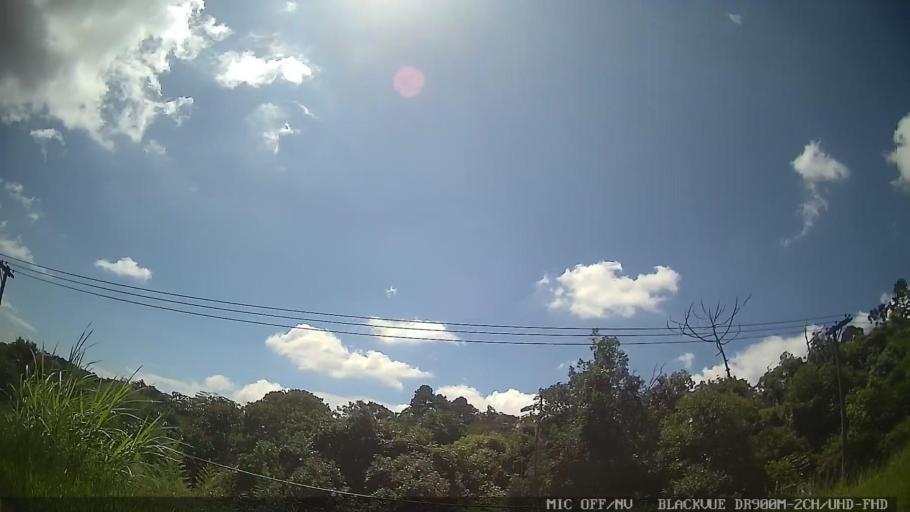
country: BR
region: Sao Paulo
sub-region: Mogi das Cruzes
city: Mogi das Cruzes
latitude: -23.6732
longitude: -46.2096
